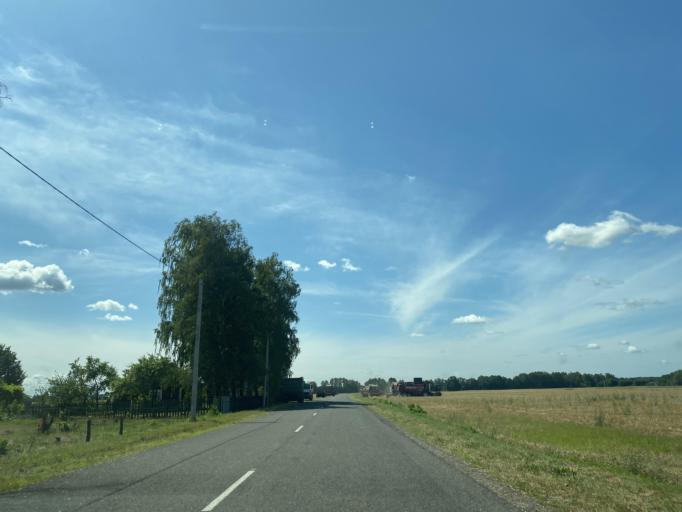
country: BY
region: Brest
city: Ivanava
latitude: 52.1975
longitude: 25.6132
